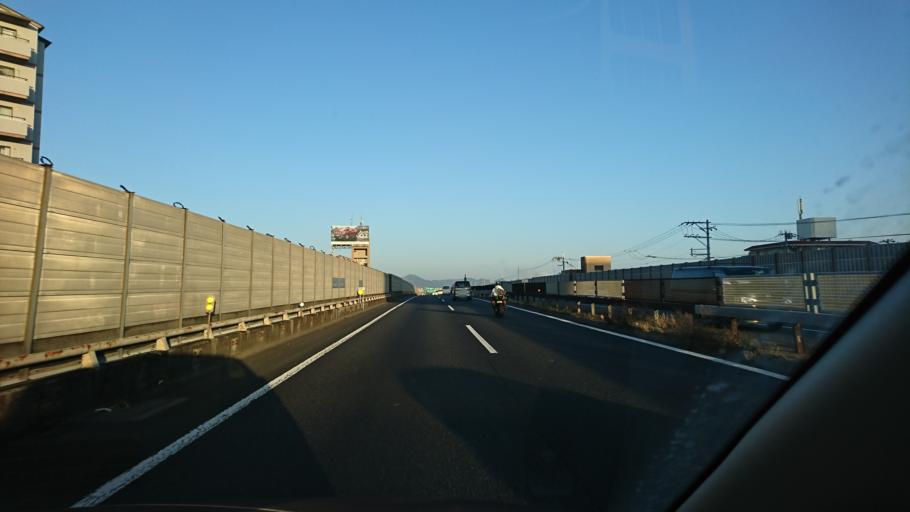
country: JP
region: Hyogo
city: Kakogawacho-honmachi
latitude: 34.7490
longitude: 134.8688
